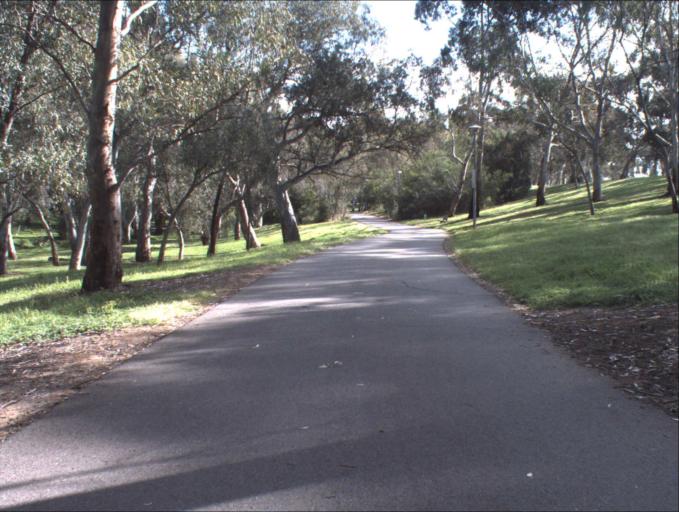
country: AU
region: South Australia
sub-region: Port Adelaide Enfield
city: Klemzig
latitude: -34.8841
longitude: 138.6451
